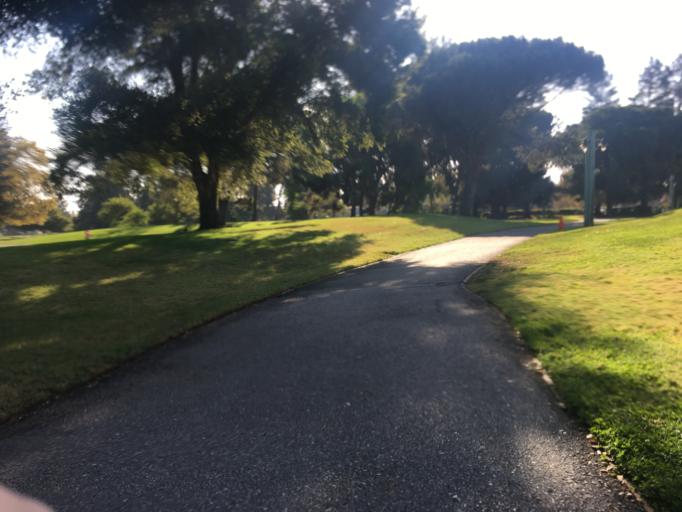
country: US
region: California
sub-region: Santa Clara County
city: Mountain View
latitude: 37.3718
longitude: -122.0810
